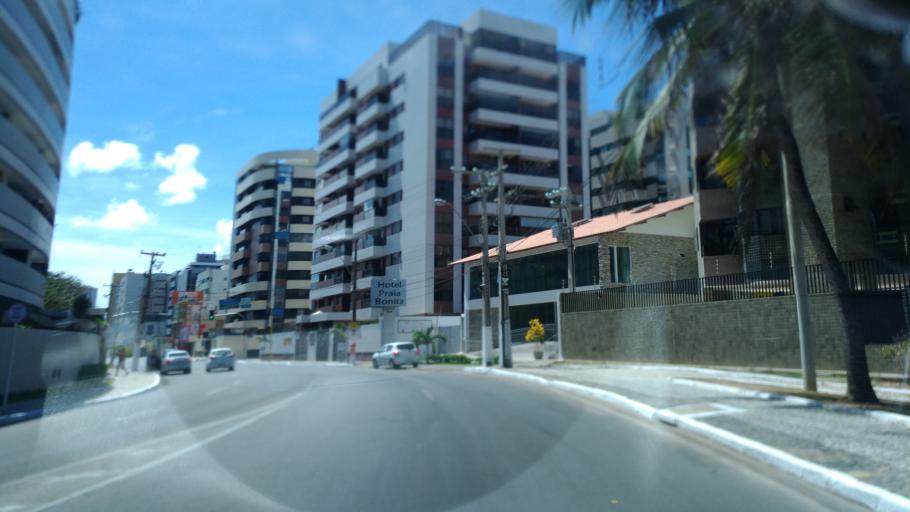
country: BR
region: Alagoas
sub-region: Maceio
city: Maceio
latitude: -9.6434
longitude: -35.6996
